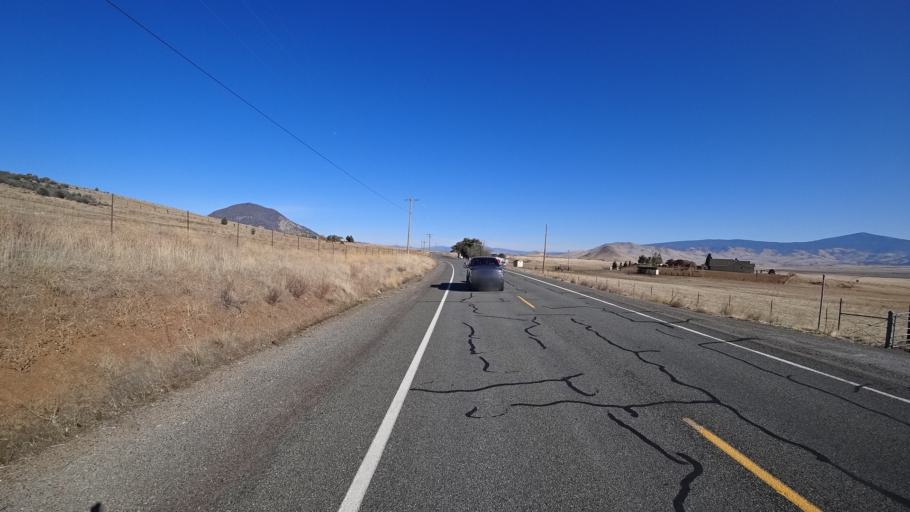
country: US
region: California
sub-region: Siskiyou County
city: Montague
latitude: 41.7998
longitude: -122.5084
